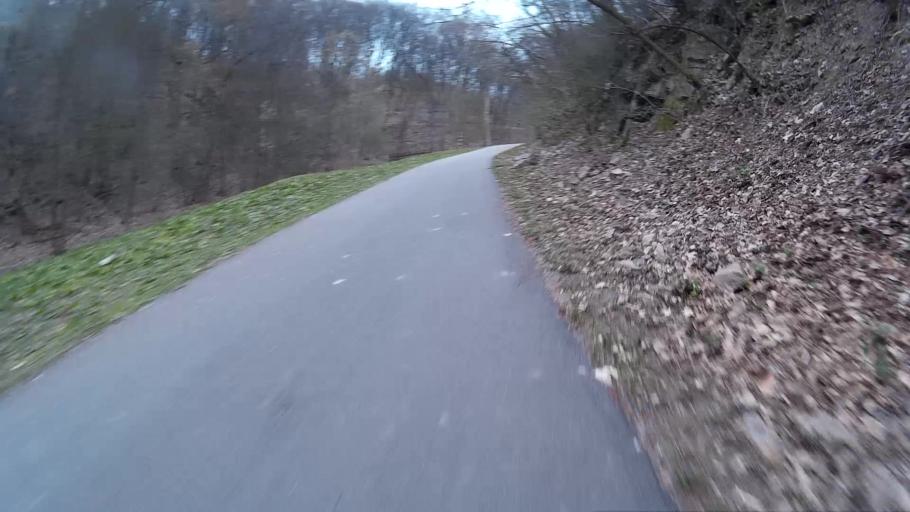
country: CZ
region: South Moravian
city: Ostopovice
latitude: 49.1845
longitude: 16.5676
